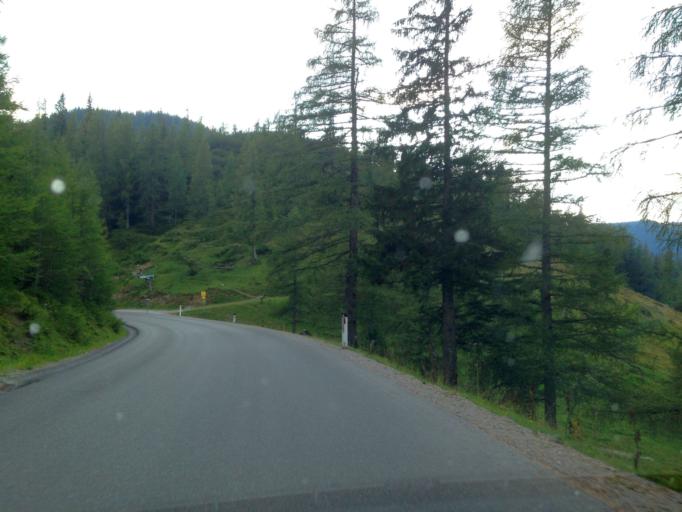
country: AT
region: Salzburg
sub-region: Politischer Bezirk Sankt Johann im Pongau
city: Filzmoos
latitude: 47.4481
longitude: 13.6079
